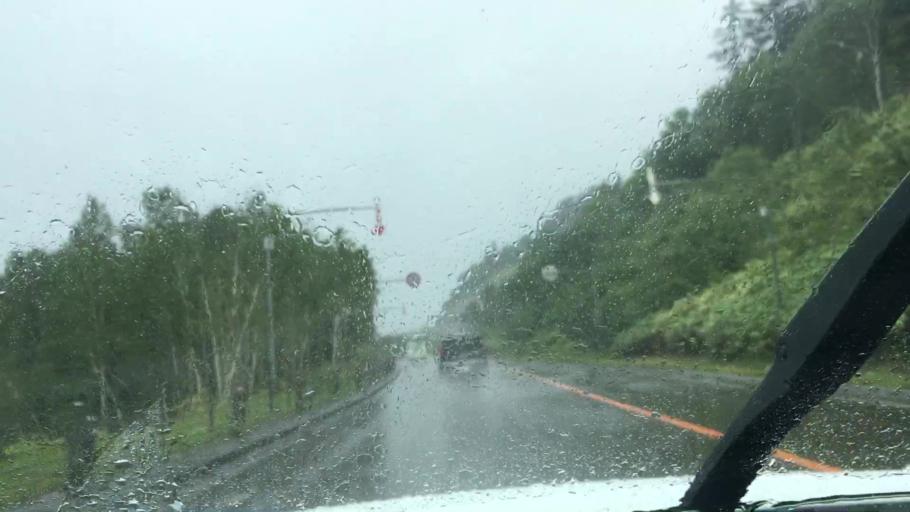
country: JP
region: Hokkaido
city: Sapporo
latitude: 42.8744
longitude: 141.1446
